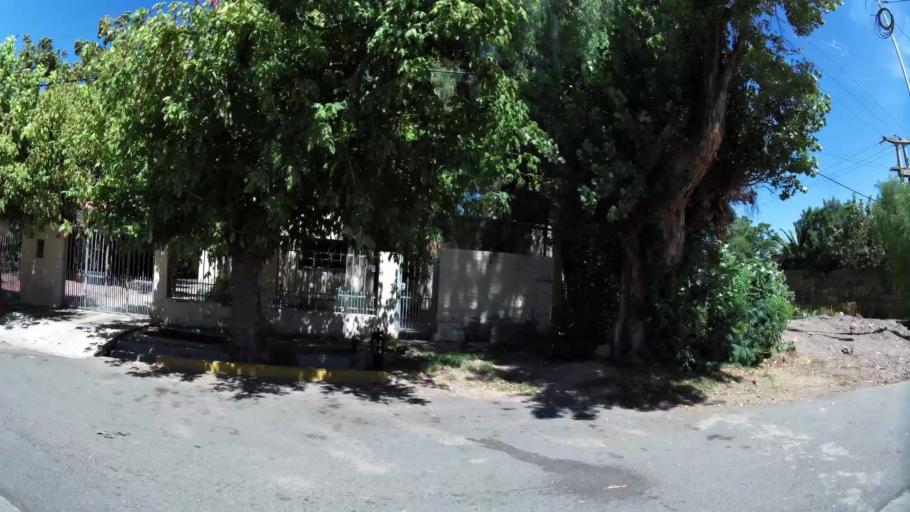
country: AR
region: Mendoza
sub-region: Departamento de Godoy Cruz
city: Godoy Cruz
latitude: -32.9617
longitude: -68.8659
